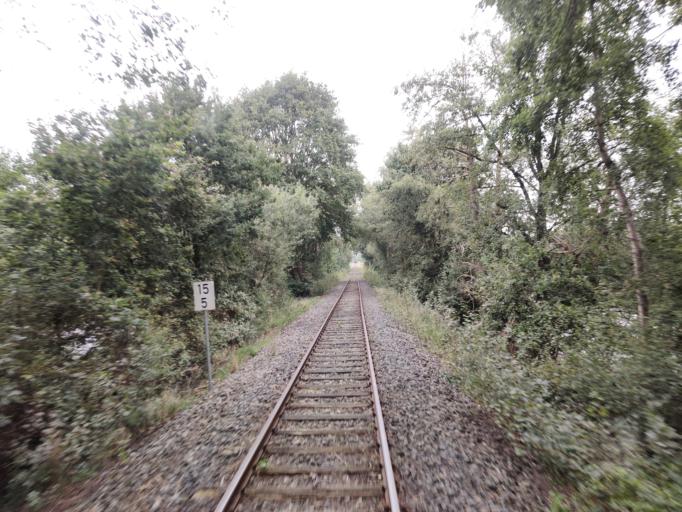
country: DE
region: Lower Saxony
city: Gnarrenburg
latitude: 53.4084
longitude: 9.0106
